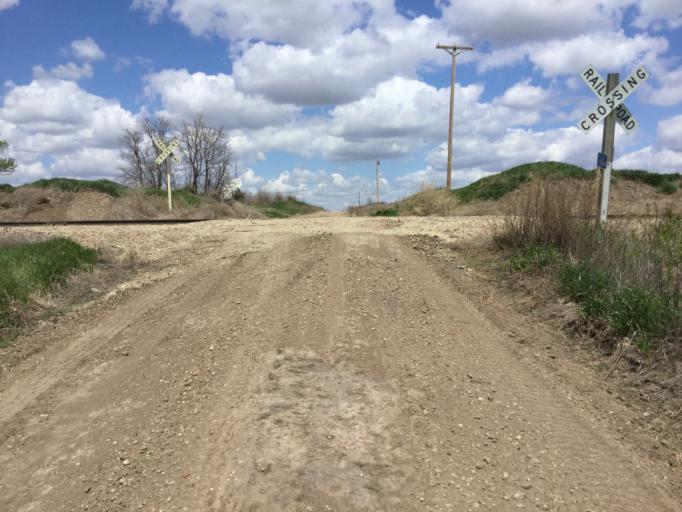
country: US
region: Kansas
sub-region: Phillips County
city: Phillipsburg
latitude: 39.7635
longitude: -99.0664
